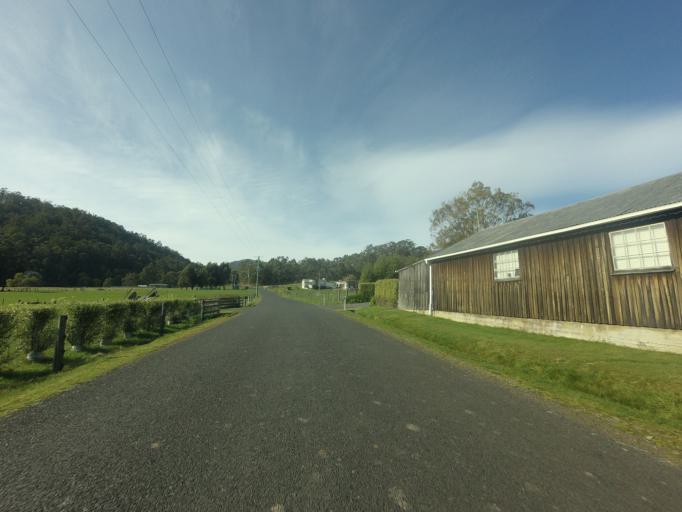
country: AU
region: Tasmania
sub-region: Huon Valley
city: Cygnet
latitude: -43.1793
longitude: 147.1343
